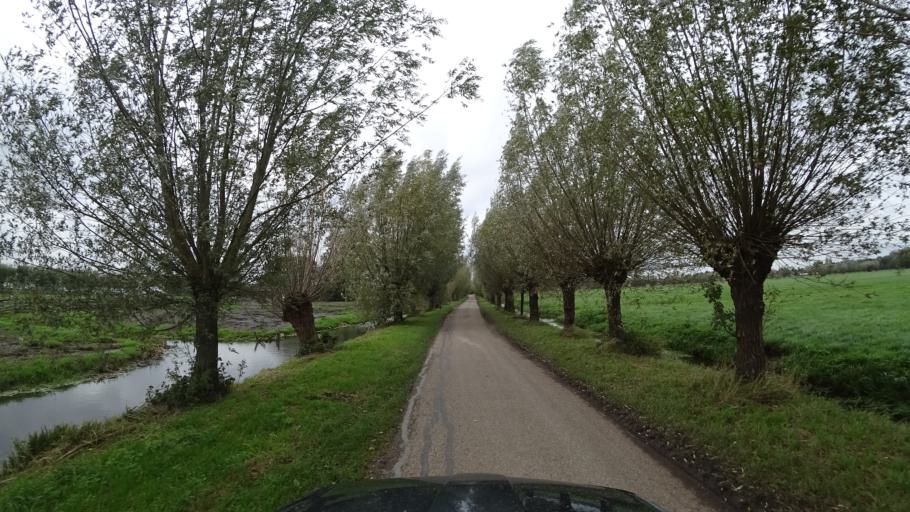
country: NL
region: Utrecht
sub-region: Stichtse Vecht
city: Spechtenkamp
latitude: 52.1524
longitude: 5.0121
